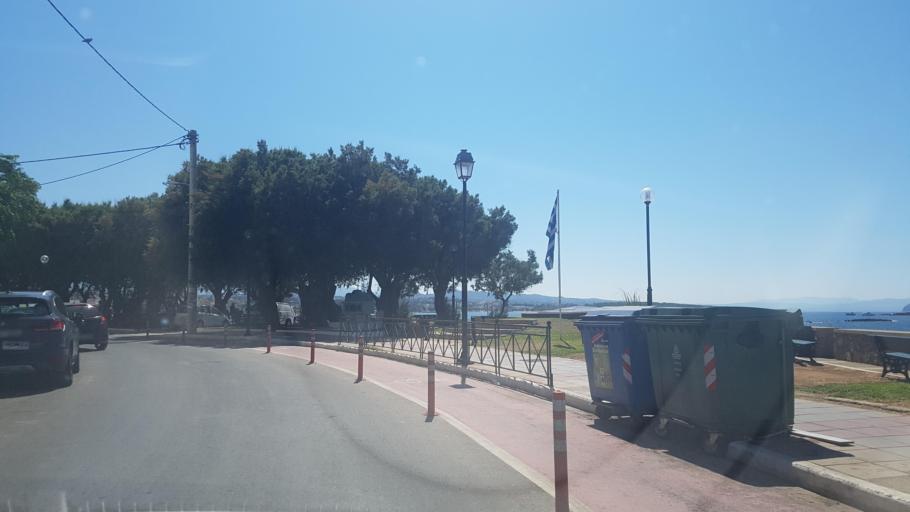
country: GR
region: Crete
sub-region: Nomos Chanias
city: Chania
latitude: 35.5171
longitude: 24.0090
